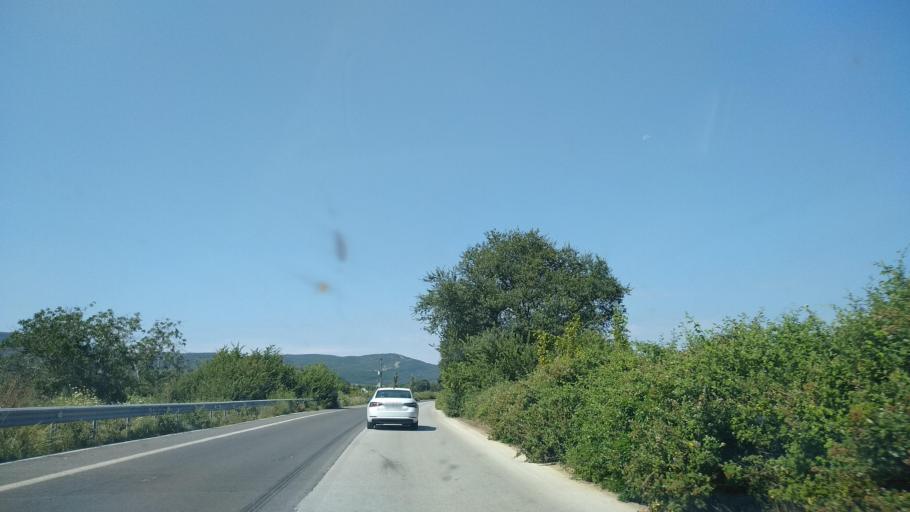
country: GR
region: Central Macedonia
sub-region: Nomos Thessalonikis
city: Stavros
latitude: 40.6444
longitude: 23.5980
